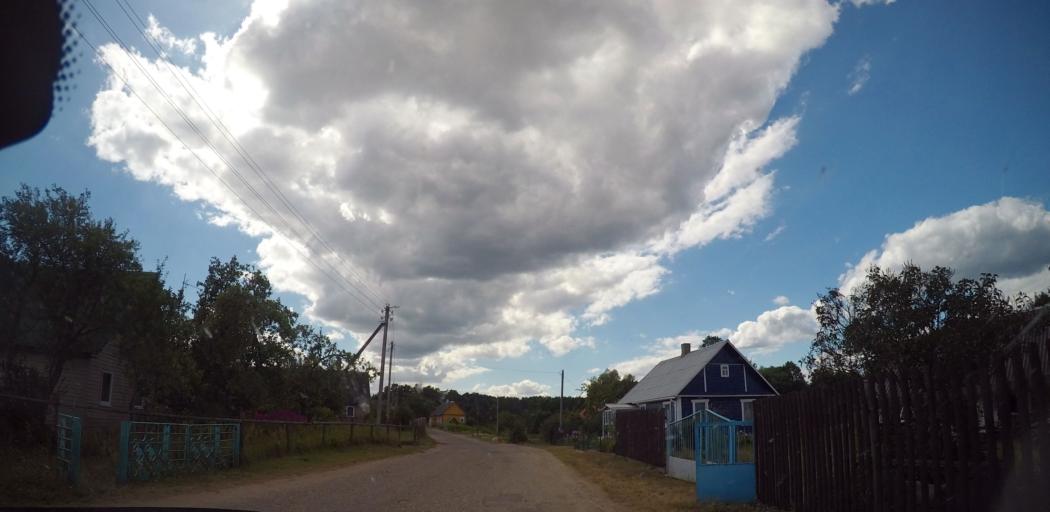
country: BY
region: Grodnenskaya
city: Skidal'
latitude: 53.8206
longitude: 24.2473
